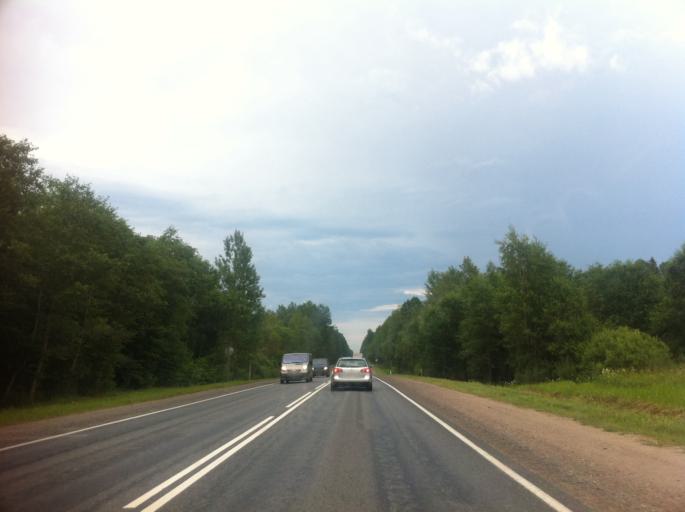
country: RU
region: Pskov
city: Strugi-Krasnyye
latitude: 58.1107
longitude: 29.1063
